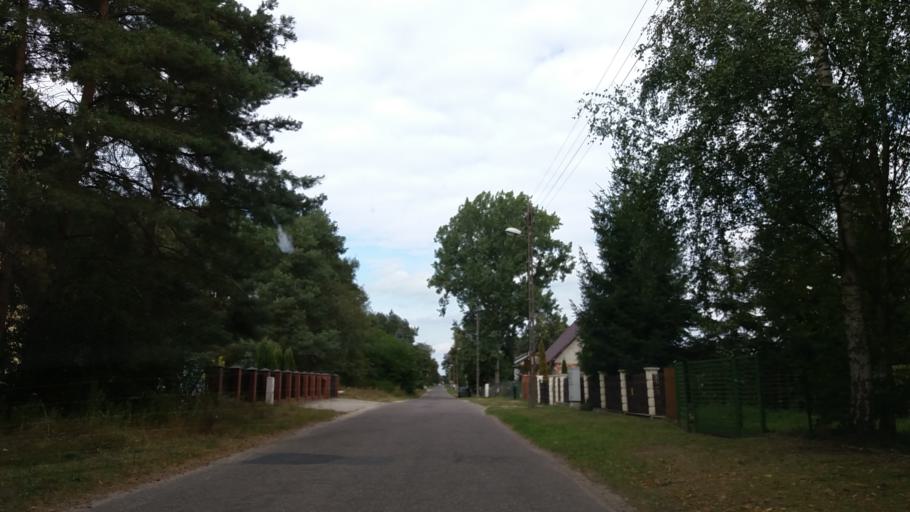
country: PL
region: West Pomeranian Voivodeship
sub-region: Powiat stargardzki
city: Kobylanka
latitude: 53.3344
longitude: 14.8911
